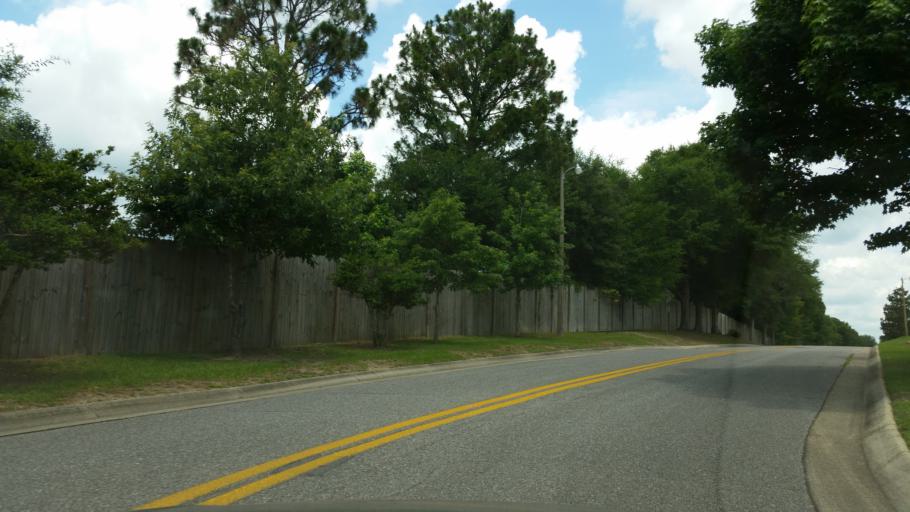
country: US
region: Florida
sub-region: Escambia County
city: Bellview
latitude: 30.4720
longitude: -87.2827
